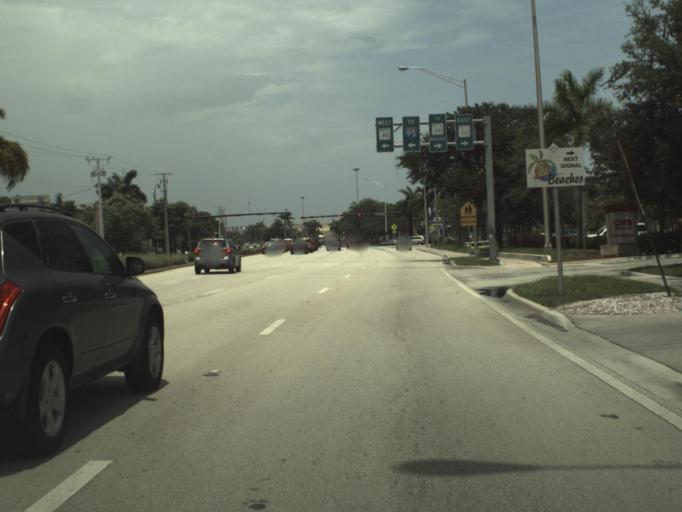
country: US
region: Florida
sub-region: Broward County
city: Deerfield Beach
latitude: 26.3164
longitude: -80.0909
